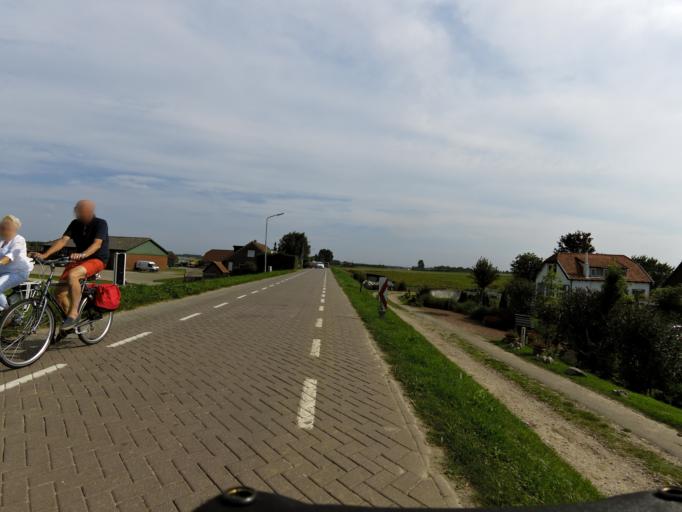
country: NL
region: South Holland
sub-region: Gemeente Zwijndrecht
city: Heerjansdam
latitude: 51.8021
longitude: 4.5758
